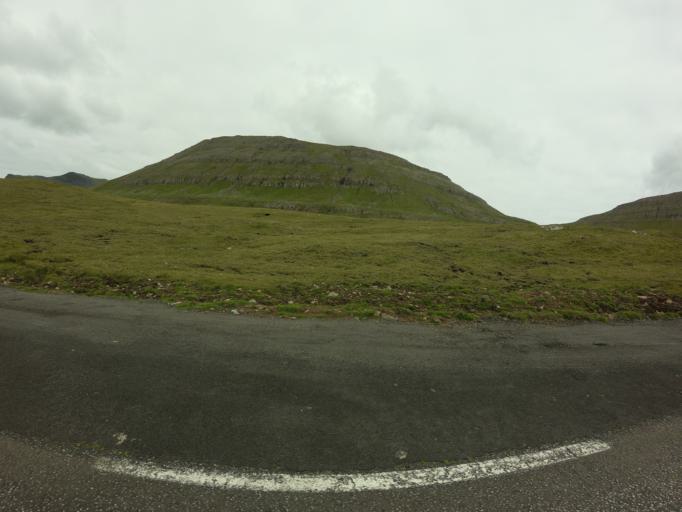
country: FO
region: Suduroy
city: Tvoroyri
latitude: 61.5190
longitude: -6.8509
